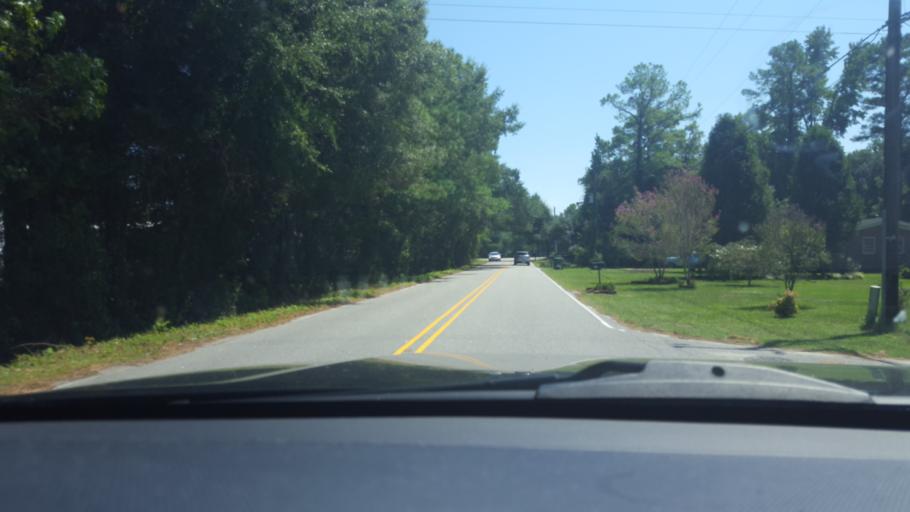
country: US
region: North Carolina
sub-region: New Hanover County
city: Ogden
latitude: 34.2571
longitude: -77.8312
